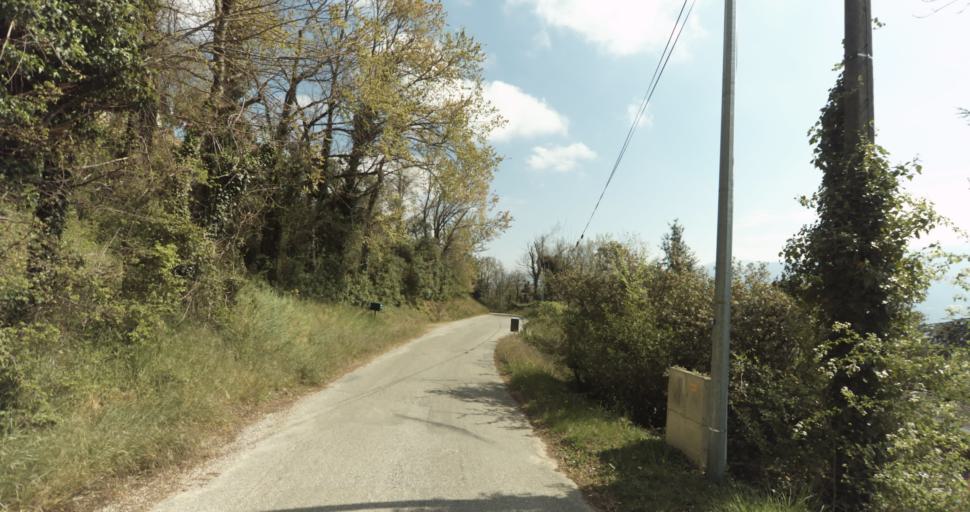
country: FR
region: Rhone-Alpes
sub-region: Departement de l'Isere
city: Saint-Marcellin
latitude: 45.1554
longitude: 5.3076
